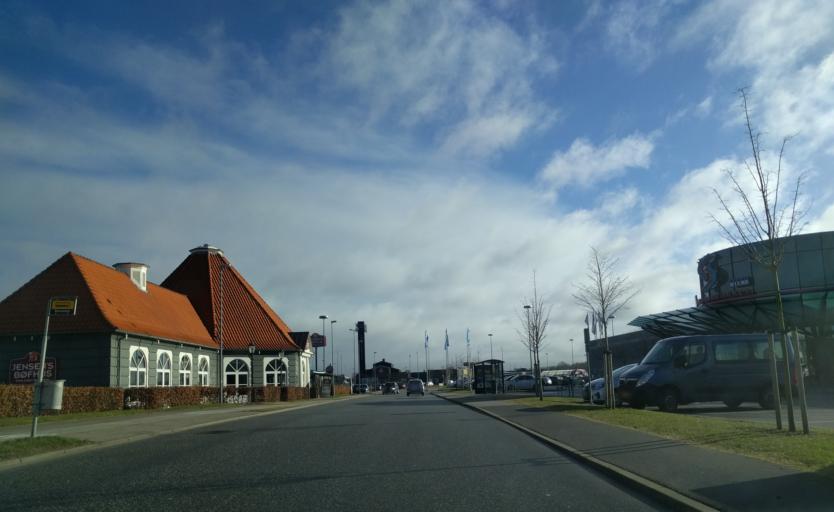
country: DK
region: North Denmark
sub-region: Alborg Kommune
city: Svenstrup
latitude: 57.0057
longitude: 9.8731
